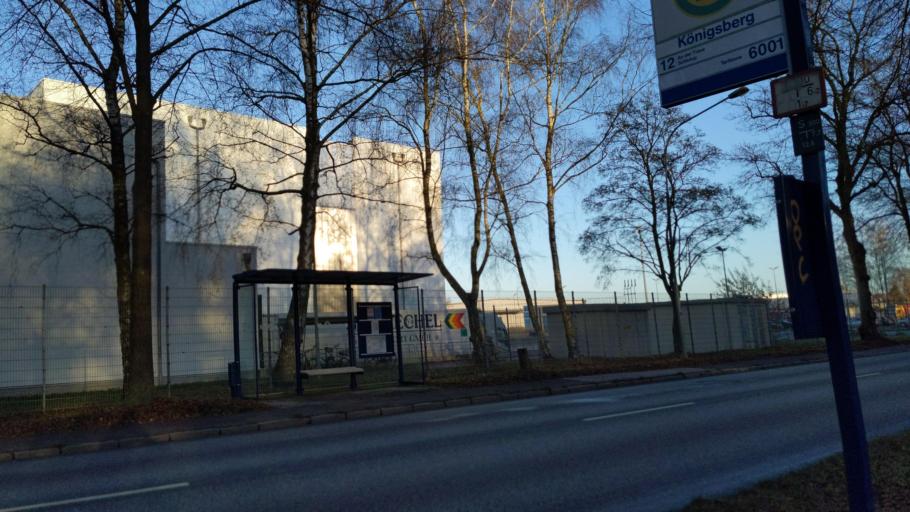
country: DE
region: Schleswig-Holstein
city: Ratekau
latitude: 53.8886
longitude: 10.7780
